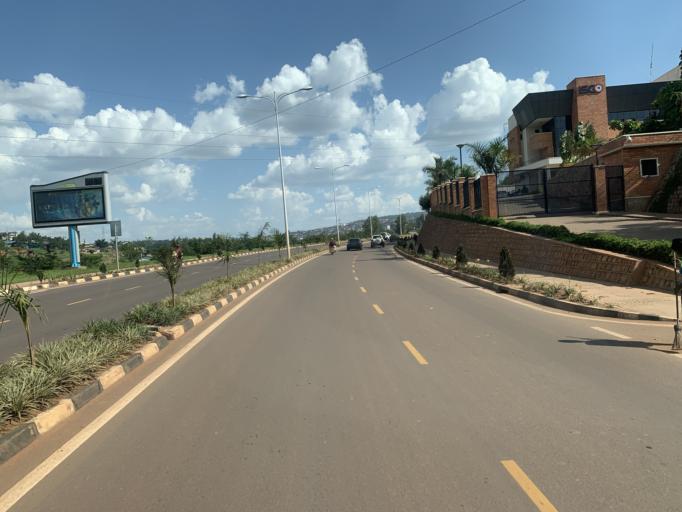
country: RW
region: Kigali
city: Kigali
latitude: -1.9574
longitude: 30.0760
